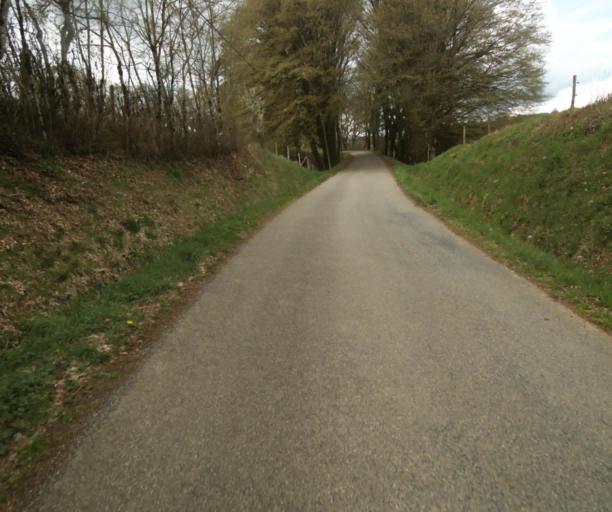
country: FR
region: Limousin
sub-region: Departement de la Correze
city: Laguenne
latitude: 45.2497
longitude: 1.8489
